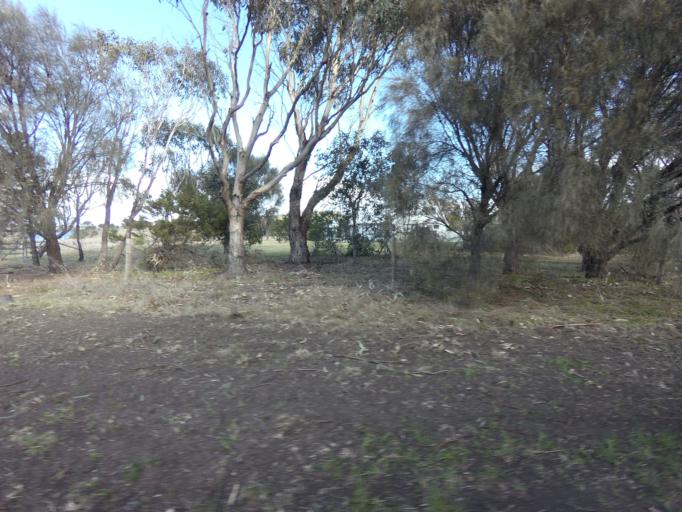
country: AU
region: Tasmania
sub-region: Sorell
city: Sorell
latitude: -42.3069
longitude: 147.9988
